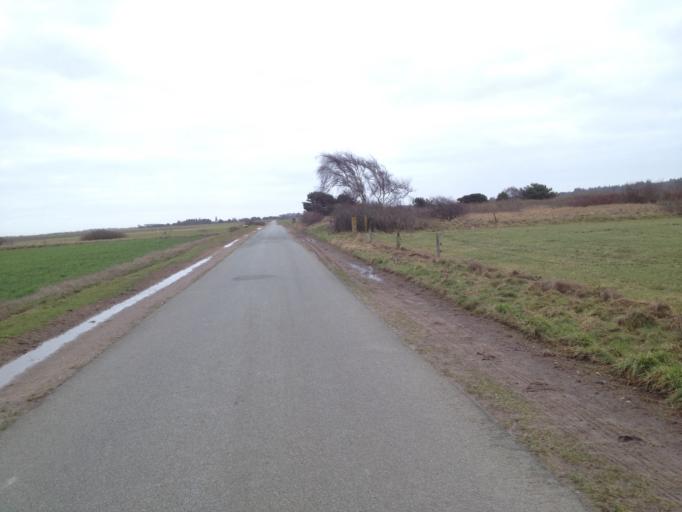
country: DE
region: Schleswig-Holstein
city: Nebel
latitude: 54.6662
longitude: 8.3448
